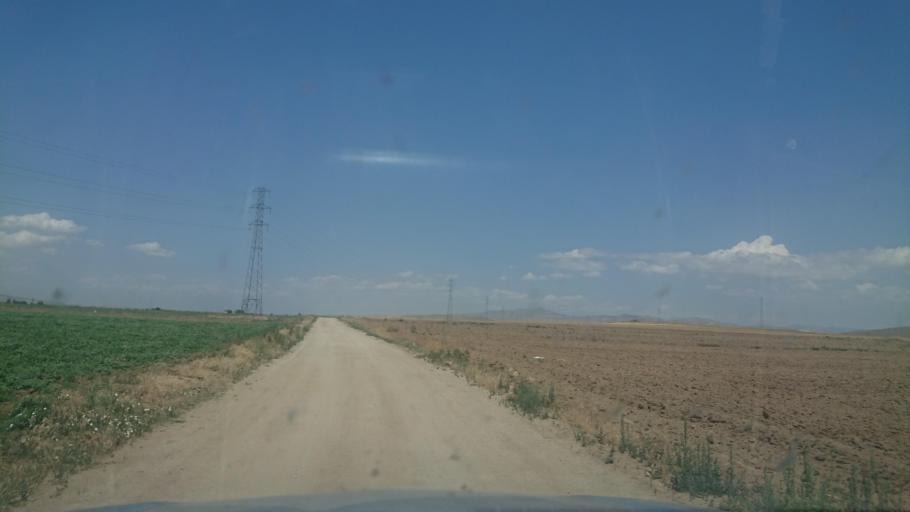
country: TR
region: Aksaray
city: Sariyahsi
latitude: 39.0098
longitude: 33.8811
